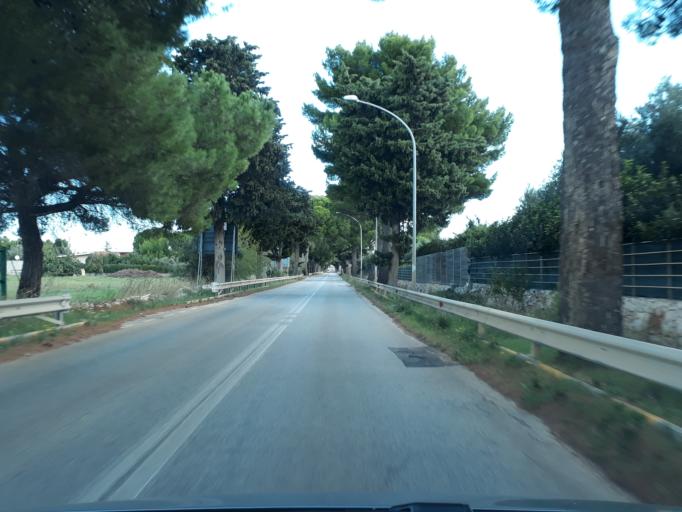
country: IT
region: Apulia
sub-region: Provincia di Bari
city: Rutigliano
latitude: 41.0289
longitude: 17.0385
